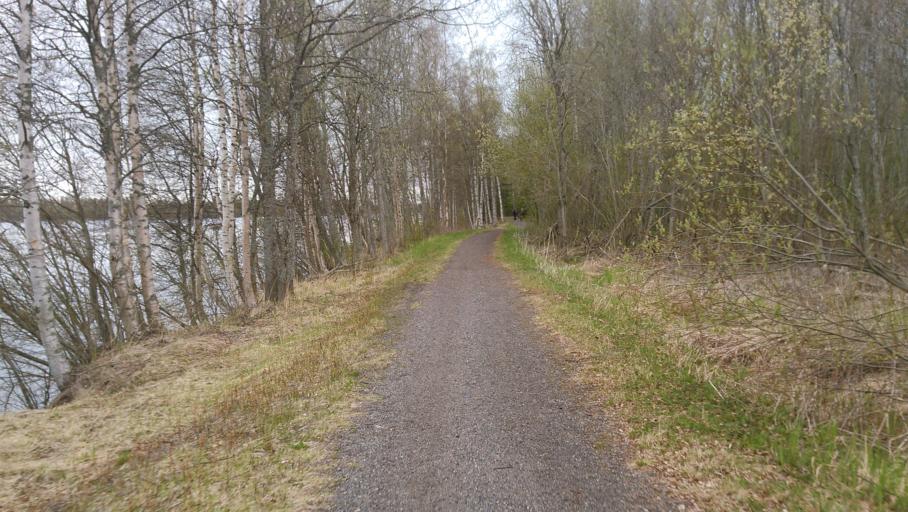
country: SE
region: Vaesterbotten
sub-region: Umea Kommun
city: Umea
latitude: 63.7812
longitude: 20.3170
